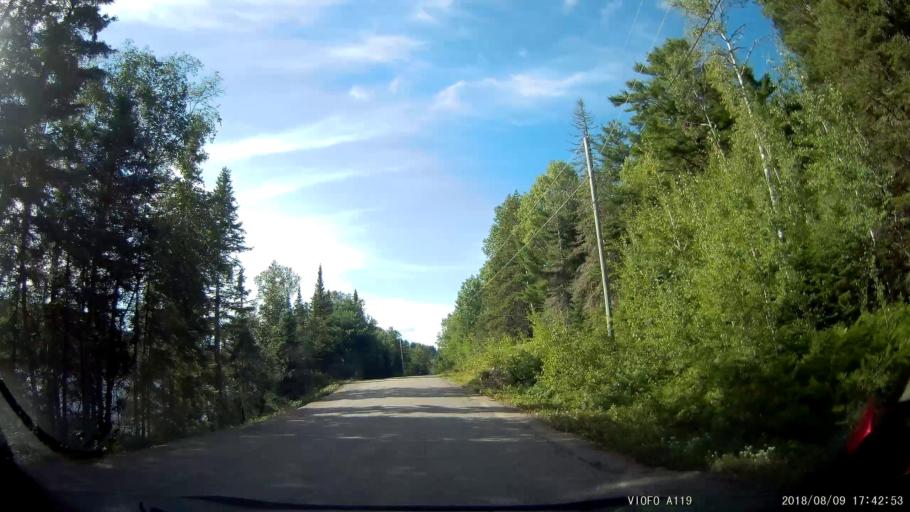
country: CA
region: Ontario
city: Rayside-Balfour
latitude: 46.6039
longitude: -81.5255
